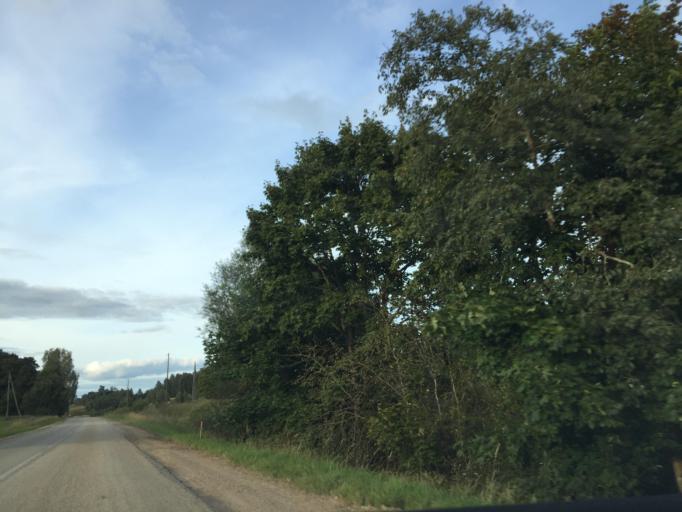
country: LV
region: Viesite
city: Viesite
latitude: 56.3065
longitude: 25.4444
